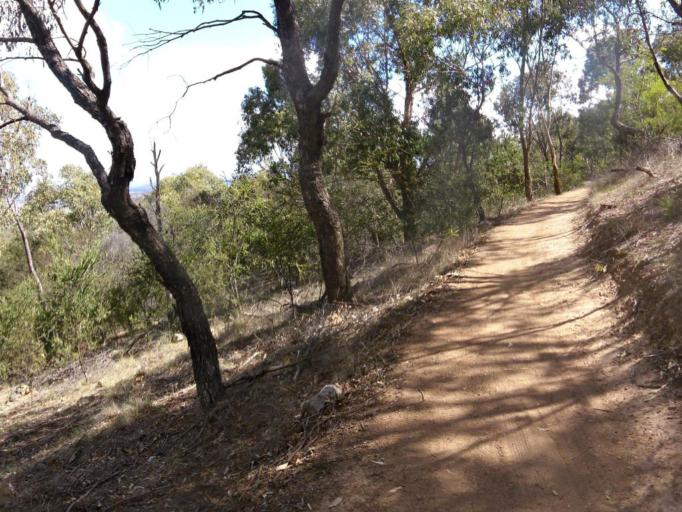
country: AU
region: Australian Capital Territory
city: Belconnen
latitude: -35.1511
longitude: 149.0876
